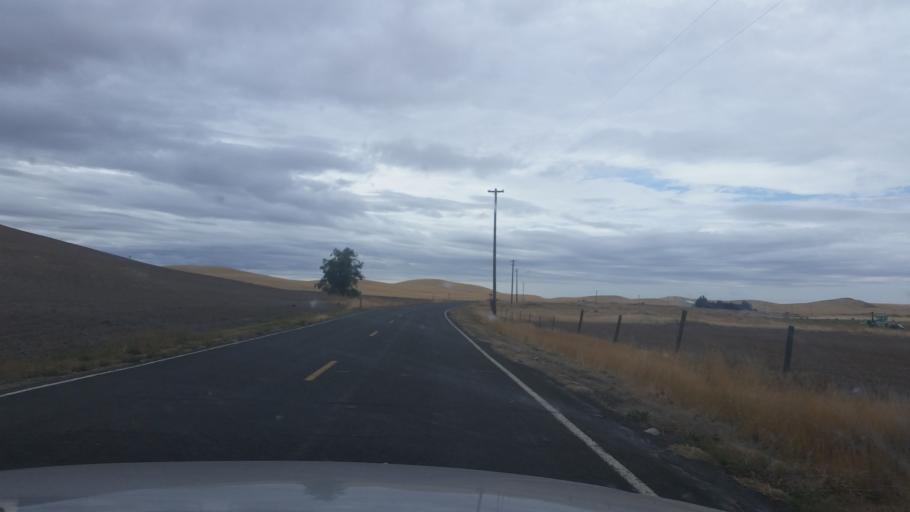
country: US
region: Washington
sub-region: Spokane County
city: Medical Lake
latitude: 47.5190
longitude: -117.8844
